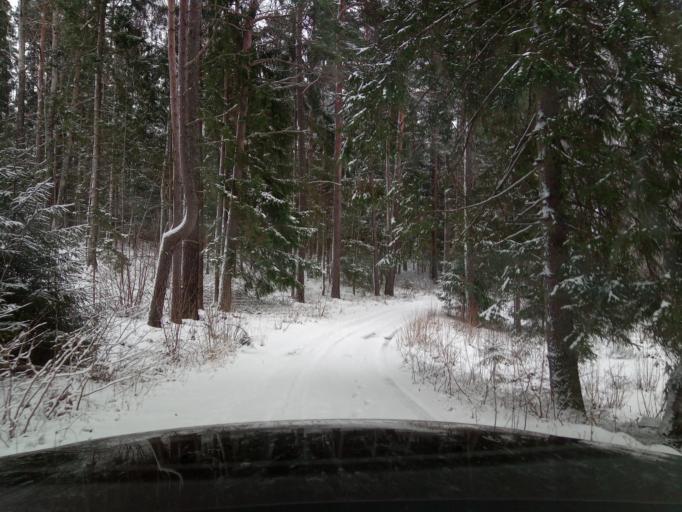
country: LT
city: Zarasai
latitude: 55.6740
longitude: 26.0259
